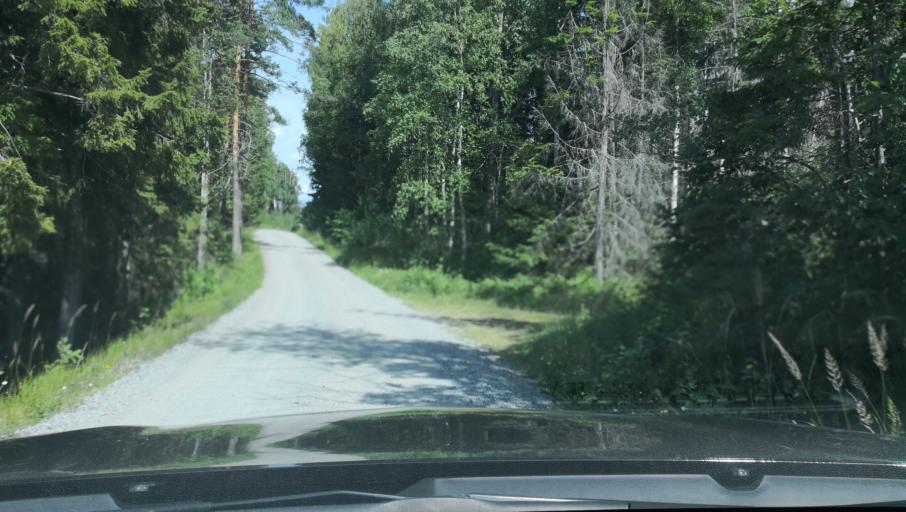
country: SE
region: Vaestmanland
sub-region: Surahammars Kommun
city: Ramnas
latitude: 59.8972
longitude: 16.1054
